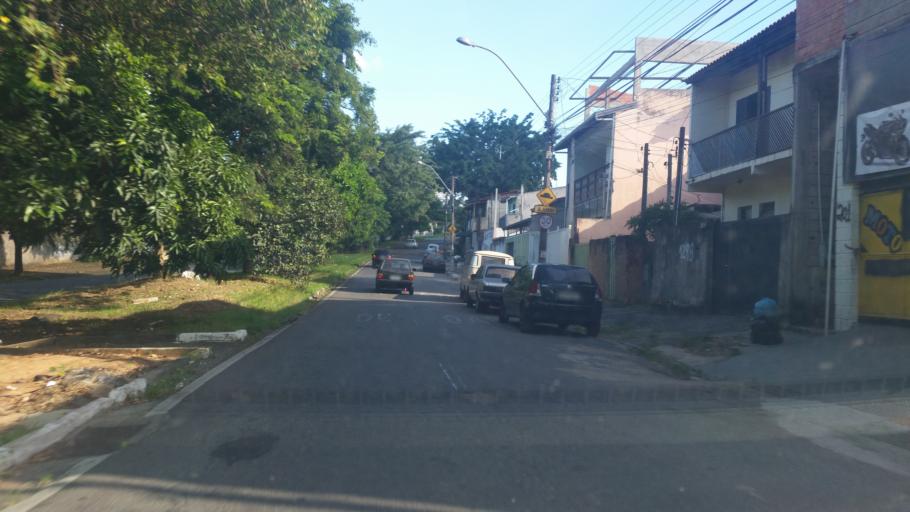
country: BR
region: Sao Paulo
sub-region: Campinas
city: Campinas
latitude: -22.8611
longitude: -47.0369
